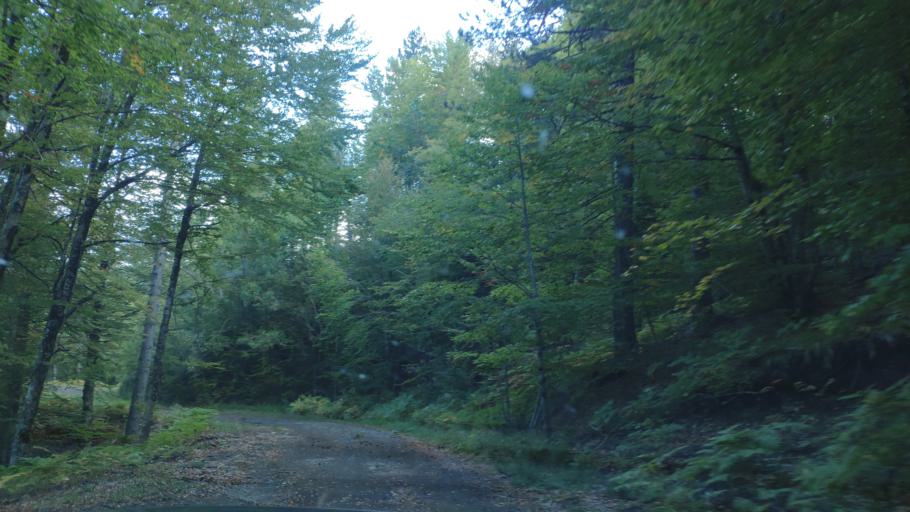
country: AL
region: Korce
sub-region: Rrethi i Devollit
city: Miras
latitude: 40.3458
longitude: 20.8993
